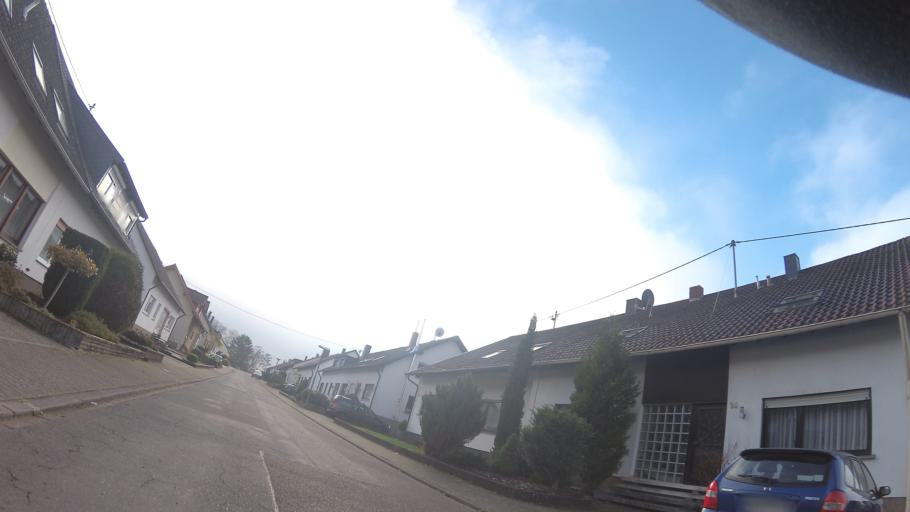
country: DE
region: Saarland
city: Ensdorf
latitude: 49.3025
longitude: 6.7842
